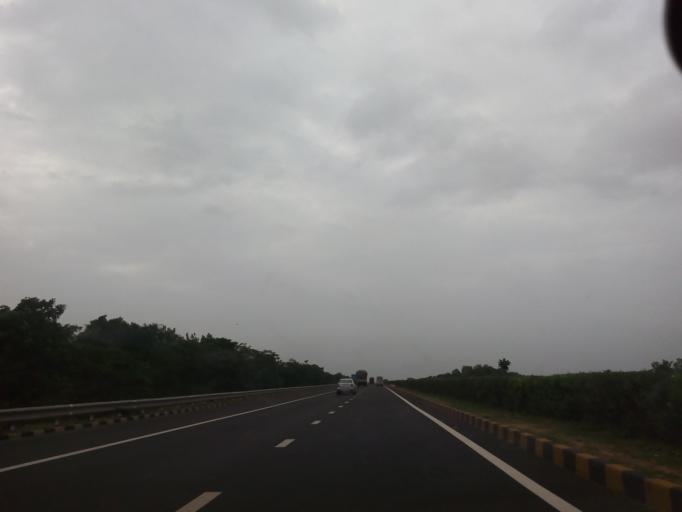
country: IN
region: Gujarat
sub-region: Kheda
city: Chaklasi
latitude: 22.6776
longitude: 72.9104
